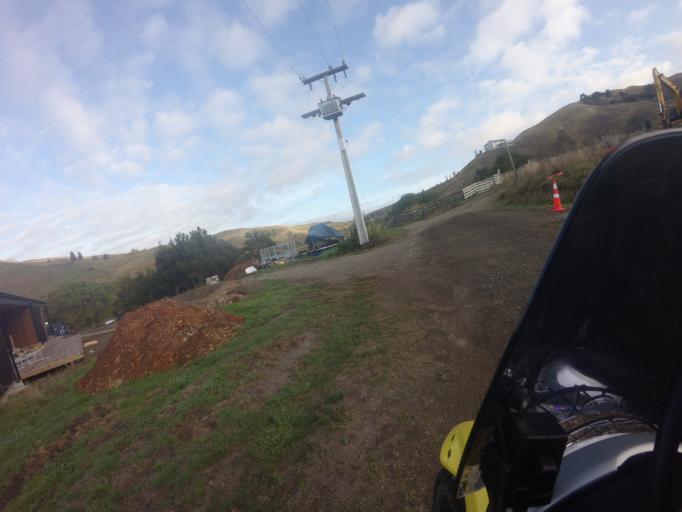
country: NZ
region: Gisborne
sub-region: Gisborne District
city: Gisborne
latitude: -38.6634
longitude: 178.0804
